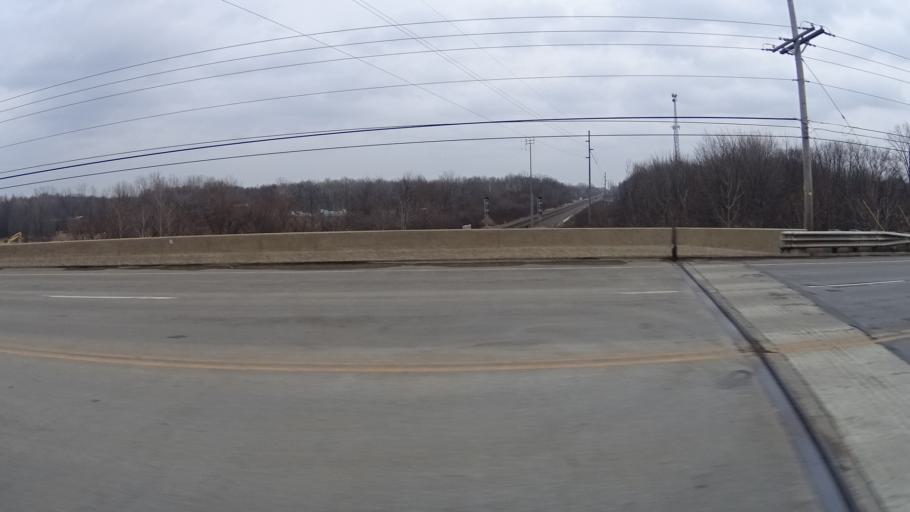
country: US
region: Ohio
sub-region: Lorain County
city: Amherst
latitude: 41.3929
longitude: -82.2099
